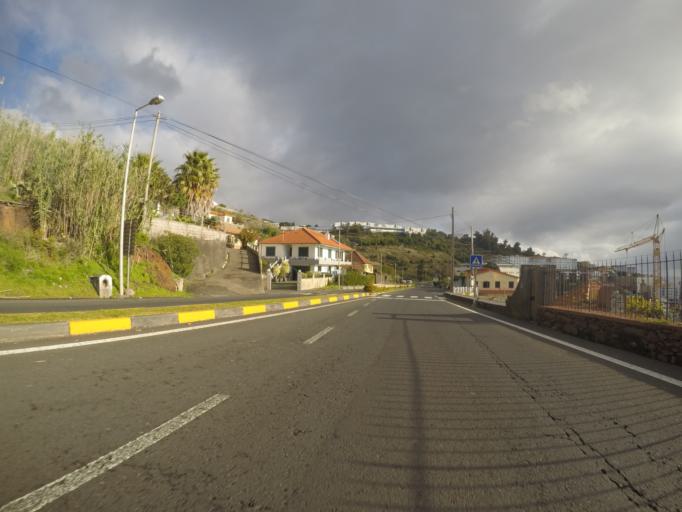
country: PT
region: Madeira
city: Canico
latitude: 32.6469
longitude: -16.8616
